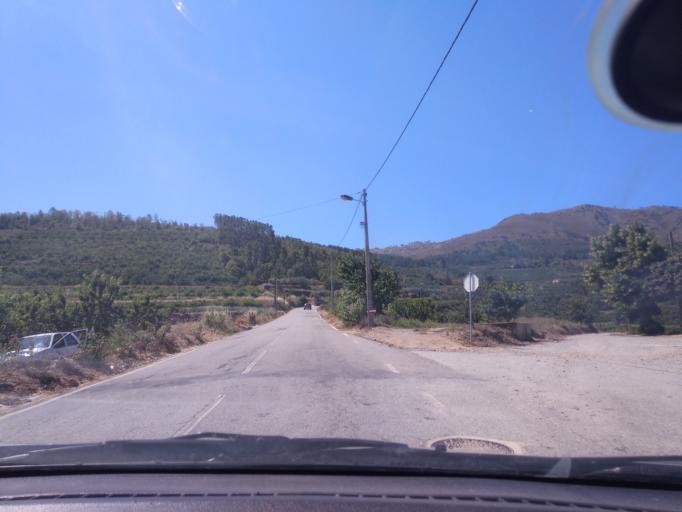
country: PT
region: Castelo Branco
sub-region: Concelho do Fundao
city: Fundao
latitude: 40.1285
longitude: -7.4871
